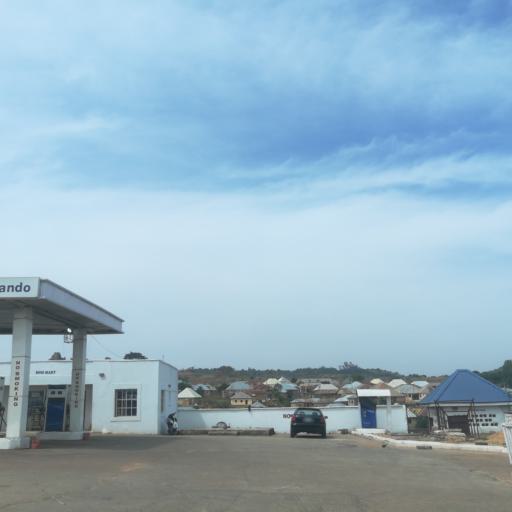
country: NG
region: Plateau
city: Jos
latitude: 9.8868
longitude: 8.8647
